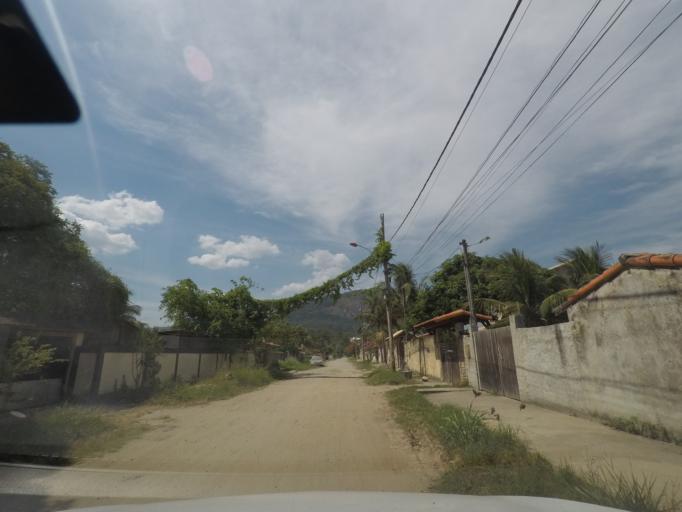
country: BR
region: Rio de Janeiro
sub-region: Marica
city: Marica
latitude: -22.9560
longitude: -42.9643
